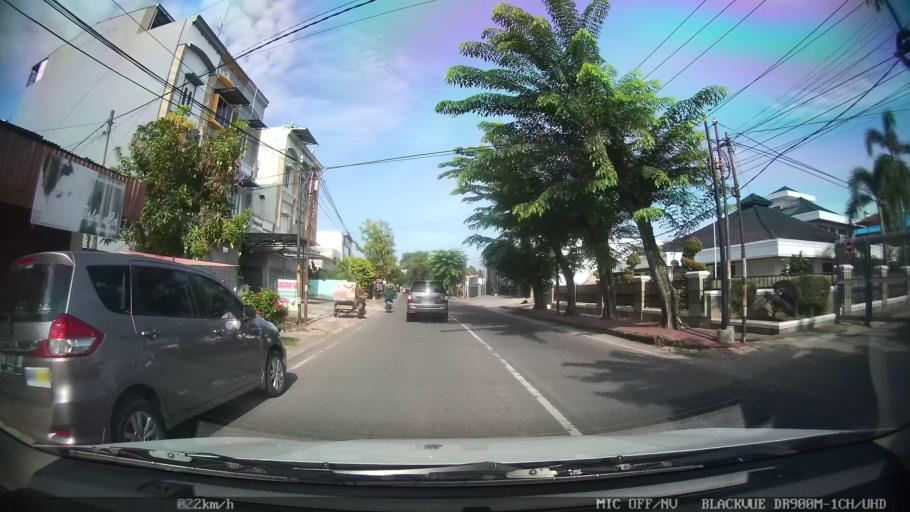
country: ID
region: North Sumatra
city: Medan
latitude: 3.6045
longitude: 98.6503
